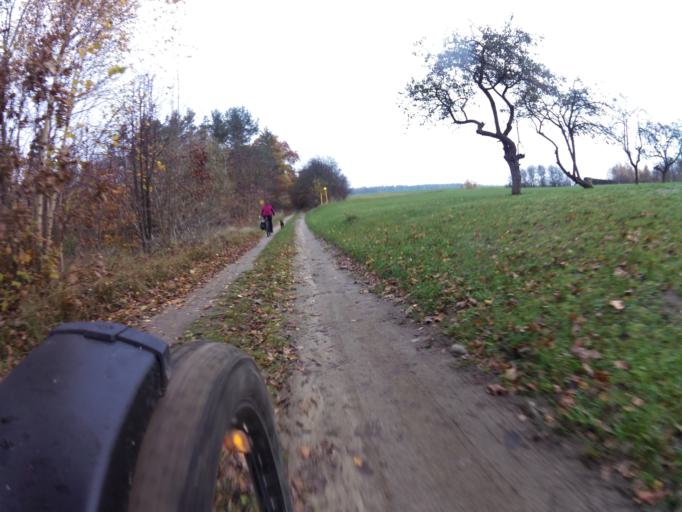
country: PL
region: Pomeranian Voivodeship
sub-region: Powiat pucki
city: Krokowa
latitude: 54.7225
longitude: 18.1329
